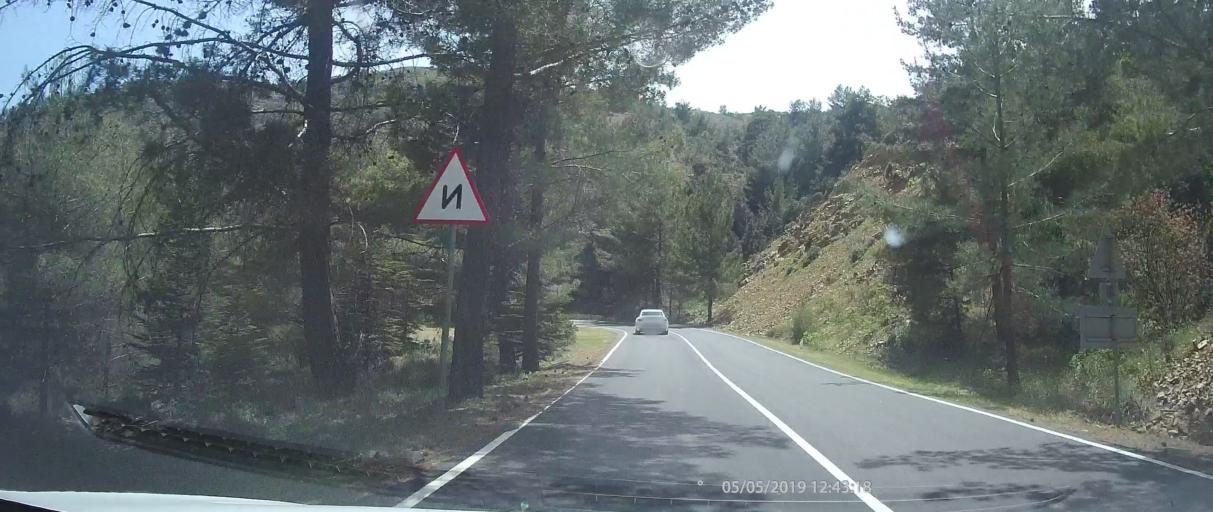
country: CY
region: Lefkosia
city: Kakopetria
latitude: 34.9689
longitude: 32.8137
